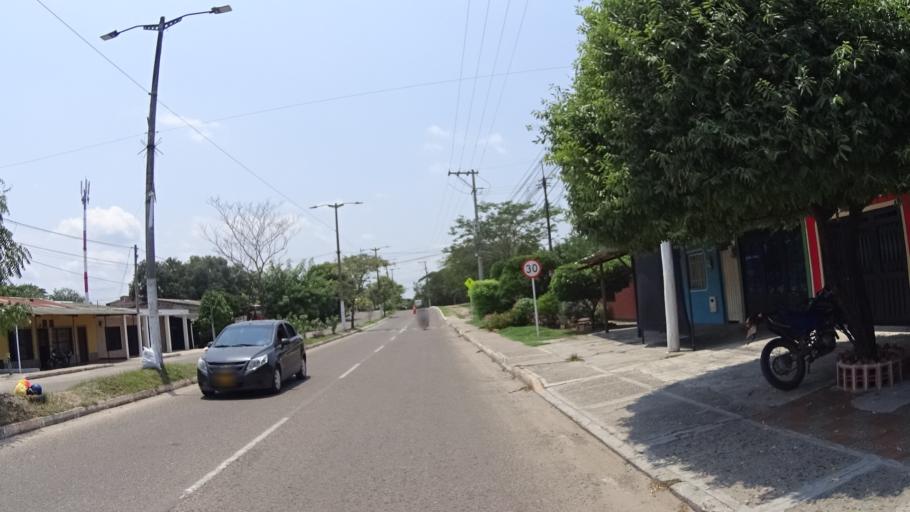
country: CO
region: Cundinamarca
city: Puerto Salgar
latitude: 5.4718
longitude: -74.6667
